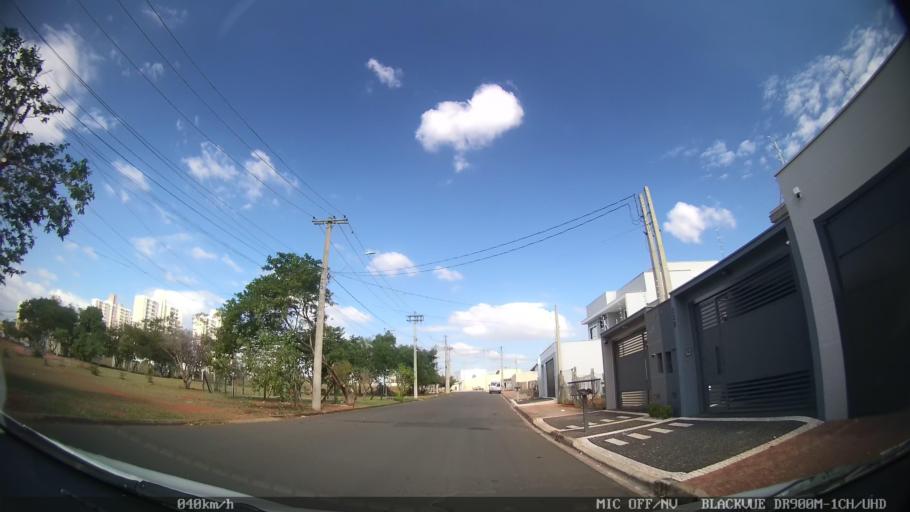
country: BR
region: Sao Paulo
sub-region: Americana
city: Americana
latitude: -22.7204
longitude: -47.3204
